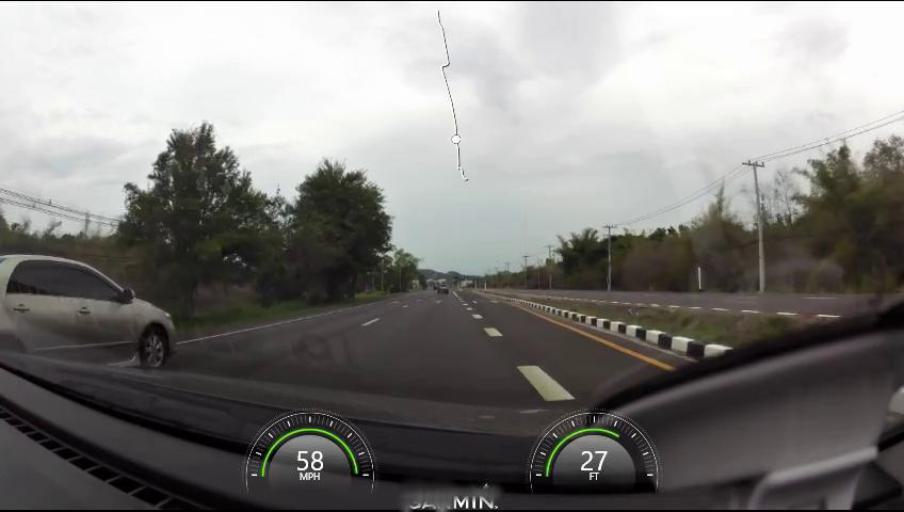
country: TH
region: Prachuap Khiri Khan
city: Hua Hin
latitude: 12.4866
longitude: 99.9701
